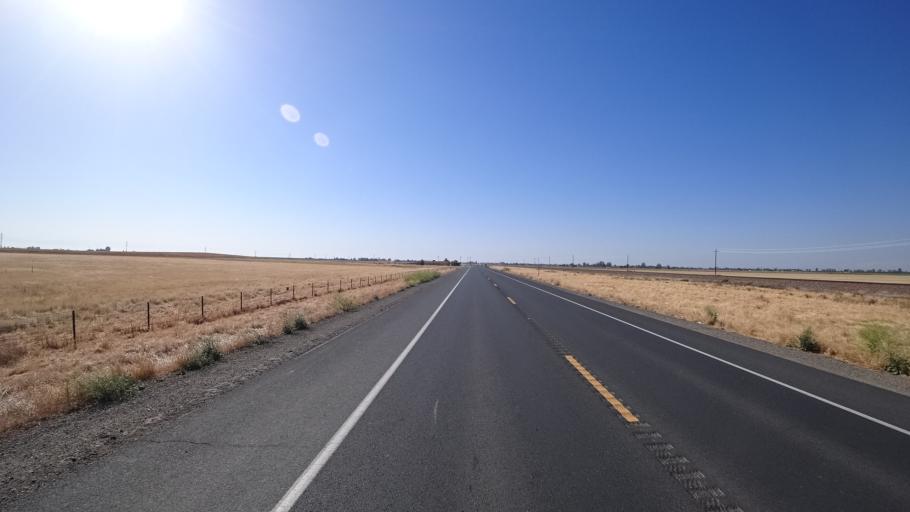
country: US
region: California
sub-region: Kings County
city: Corcoran
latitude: 36.1336
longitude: -119.5819
